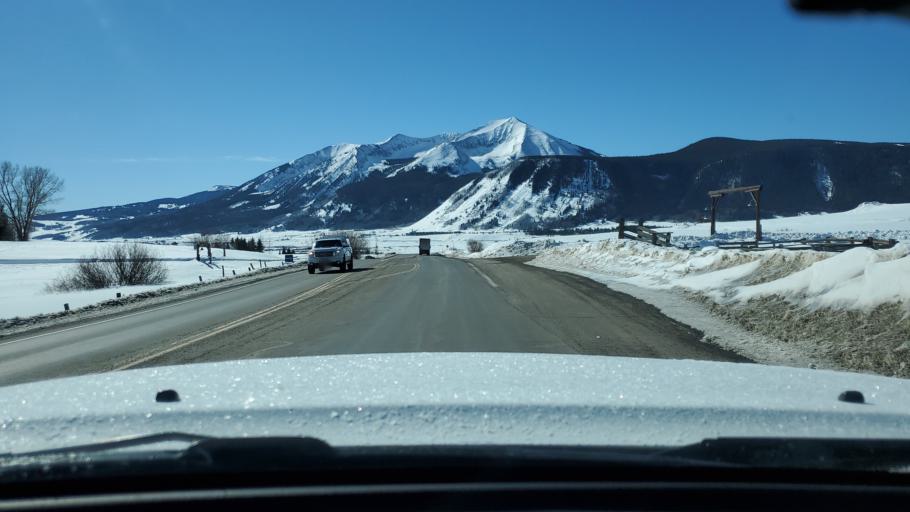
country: US
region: Colorado
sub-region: Gunnison County
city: Crested Butte
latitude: 38.8883
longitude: -106.9715
